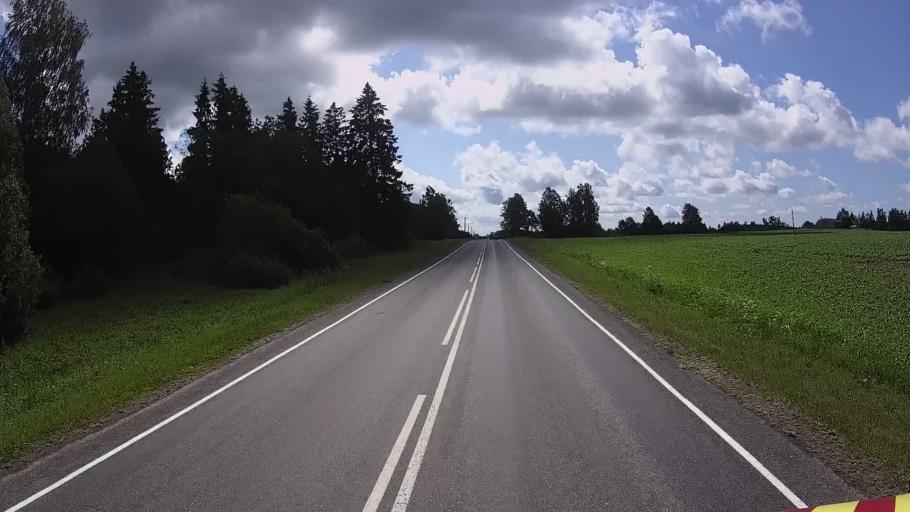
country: EE
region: Viljandimaa
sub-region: Viiratsi vald
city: Viiratsi
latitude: 58.3029
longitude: 25.6788
